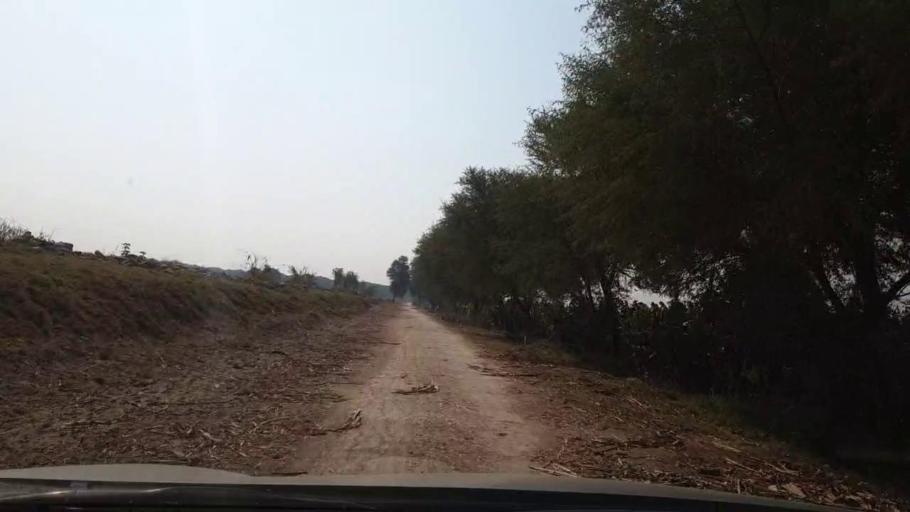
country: PK
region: Sindh
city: Tando Allahyar
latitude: 25.5022
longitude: 68.7860
